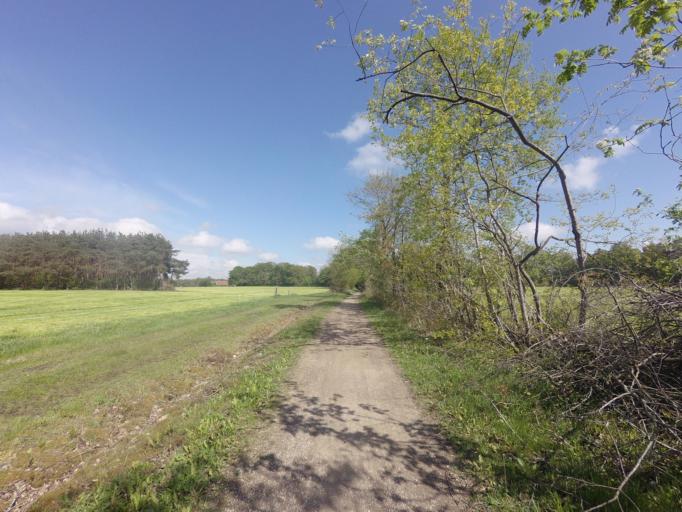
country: NL
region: Overijssel
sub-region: Gemeente Haaksbergen
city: Haaksbergen
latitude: 52.1659
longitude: 6.7926
